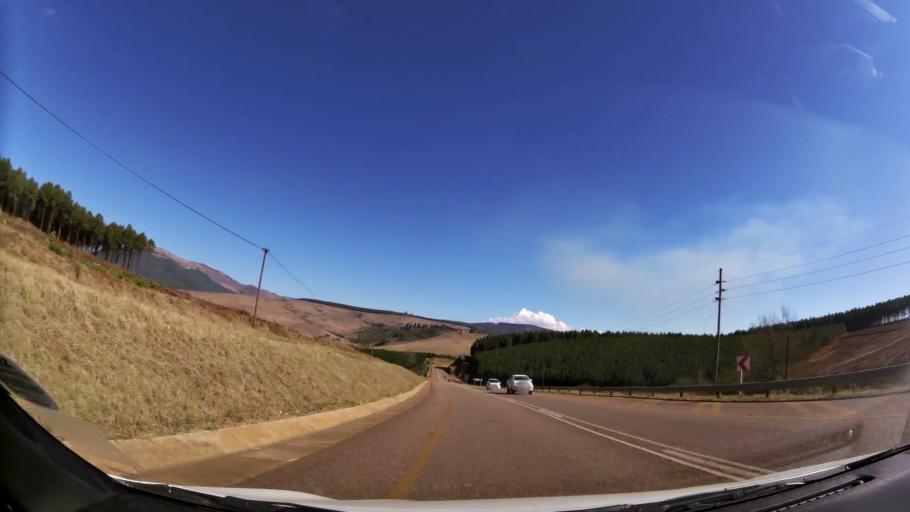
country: ZA
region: Limpopo
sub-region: Capricorn District Municipality
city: Mankoeng
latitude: -23.9356
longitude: 29.9534
